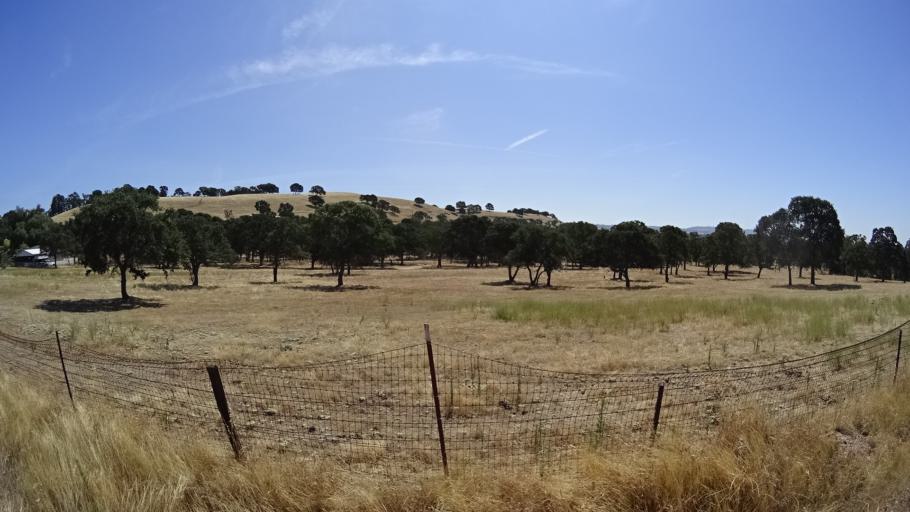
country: US
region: California
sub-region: Calaveras County
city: Rancho Calaveras
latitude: 38.1246
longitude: -120.9086
